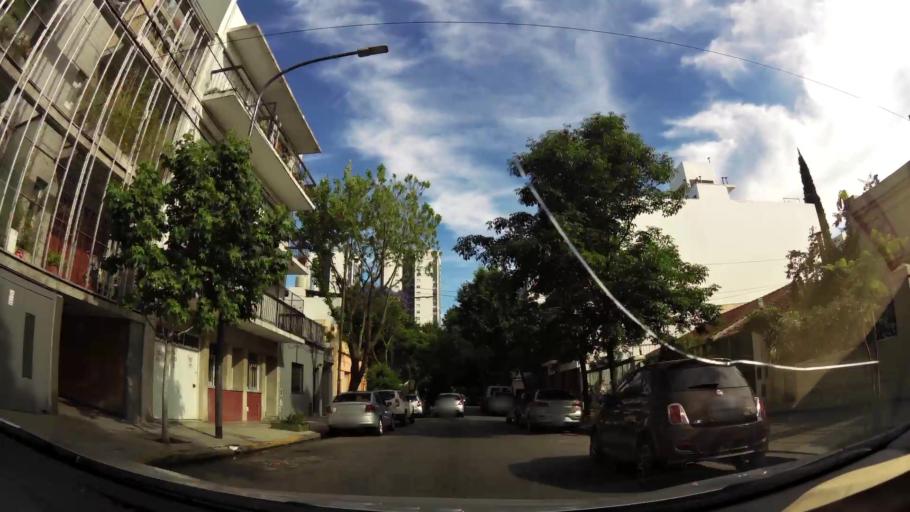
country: AR
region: Buenos Aires F.D.
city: Colegiales
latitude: -34.5523
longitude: -58.4859
